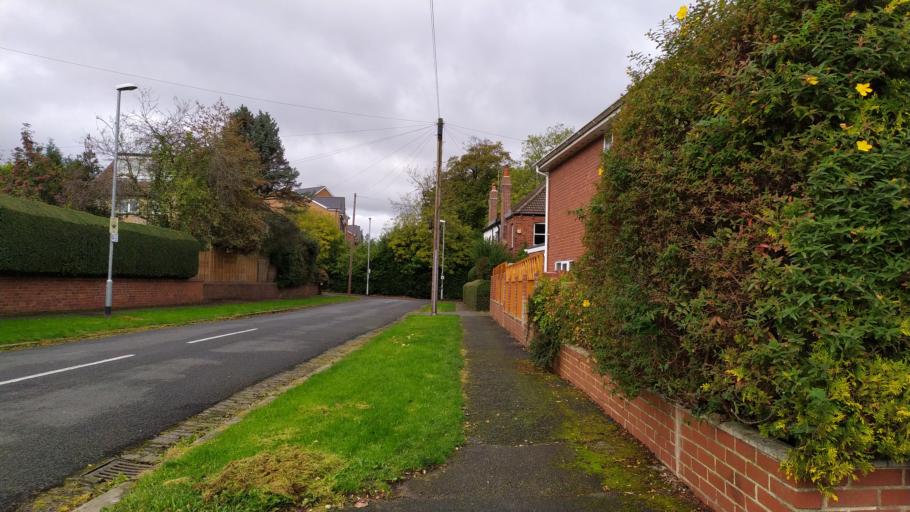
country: GB
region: England
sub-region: City and Borough of Leeds
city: Chapel Allerton
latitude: 53.8289
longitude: -1.5873
